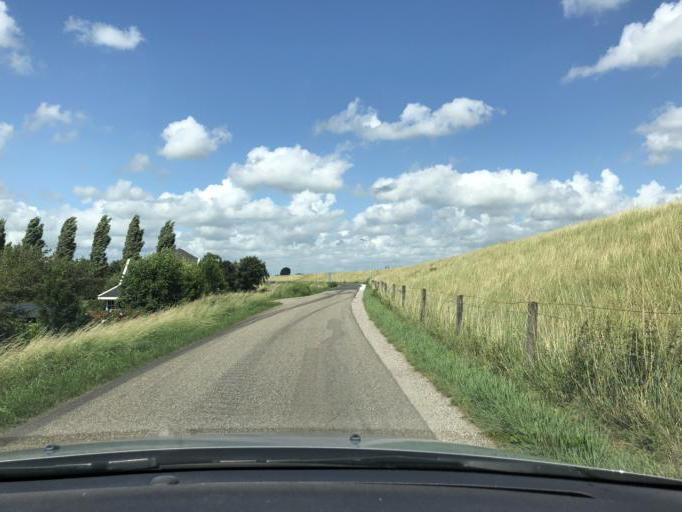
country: NL
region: North Holland
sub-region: Gemeente Hoorn
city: Hoorn
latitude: 52.6117
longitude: 5.0193
